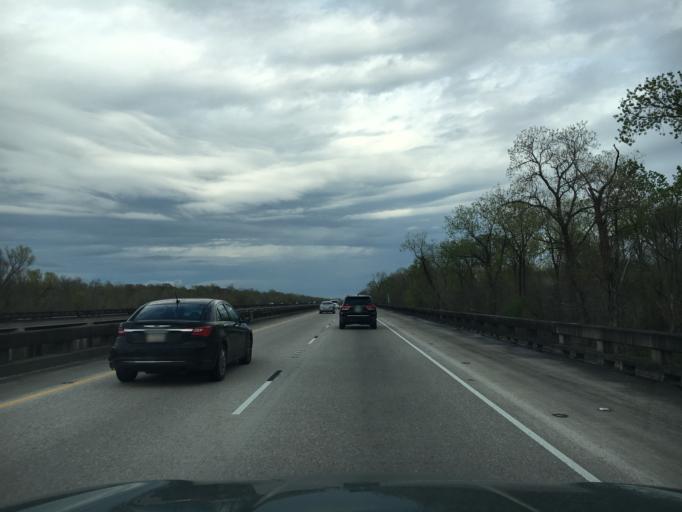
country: US
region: Louisiana
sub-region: Iberville Parish
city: Maringouin
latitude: 30.3723
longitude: -91.6113
